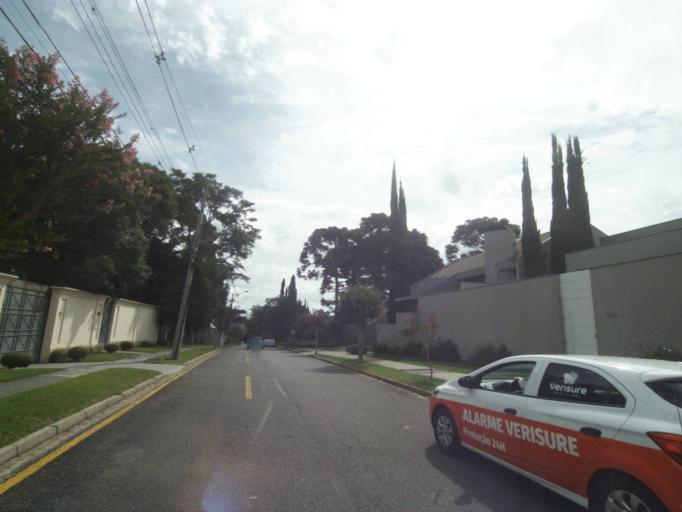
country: BR
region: Parana
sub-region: Curitiba
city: Curitiba
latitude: -25.4455
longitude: -49.3018
